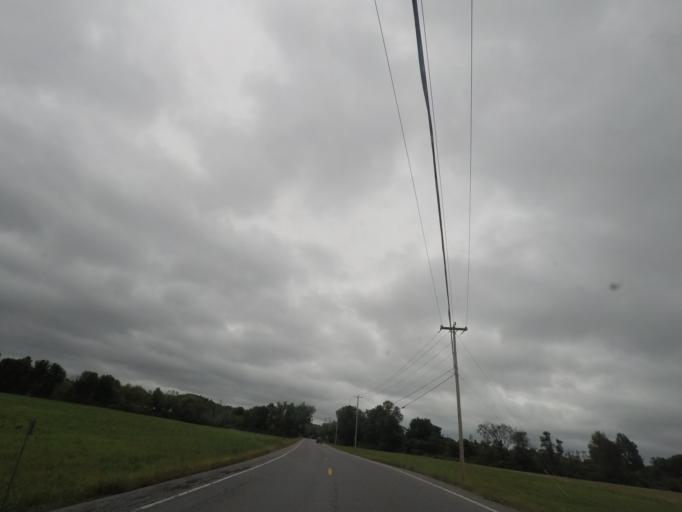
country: US
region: New York
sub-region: Saratoga County
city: Country Knolls
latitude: 42.9388
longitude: -73.7725
